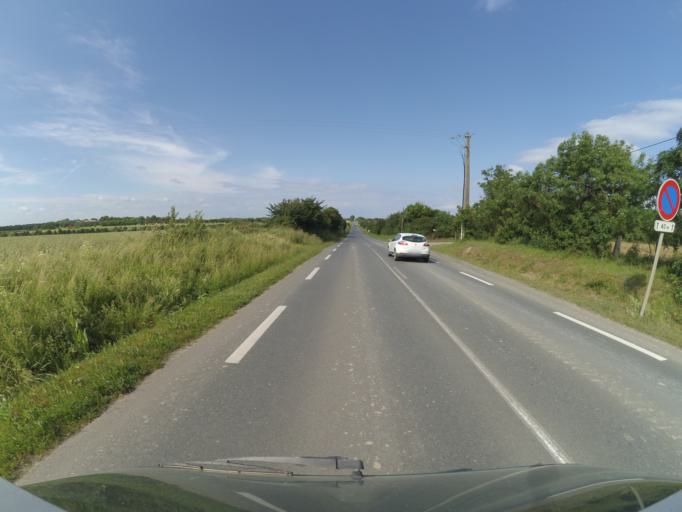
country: FR
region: Poitou-Charentes
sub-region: Departement de la Charente-Maritime
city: Saint-Xandre
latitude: 46.2271
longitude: -1.0814
